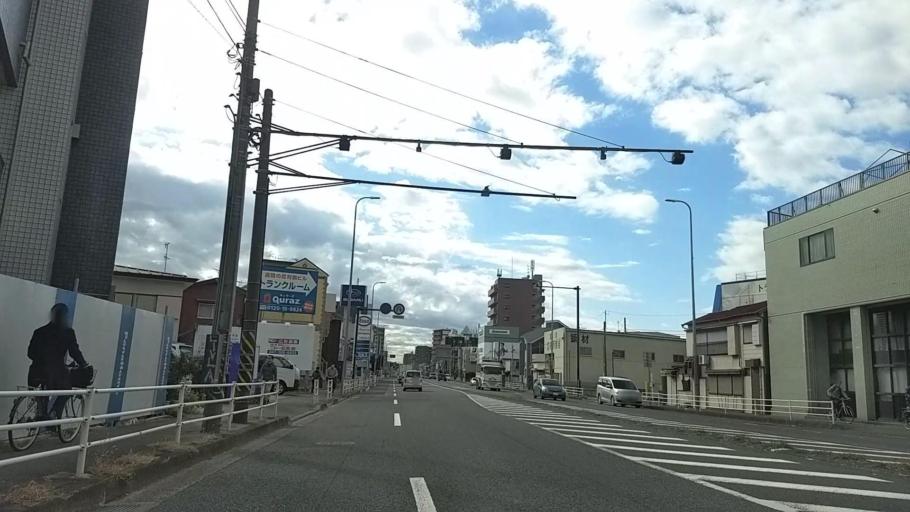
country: JP
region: Kanagawa
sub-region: Kawasaki-shi
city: Kawasaki
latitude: 35.5428
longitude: 139.6907
